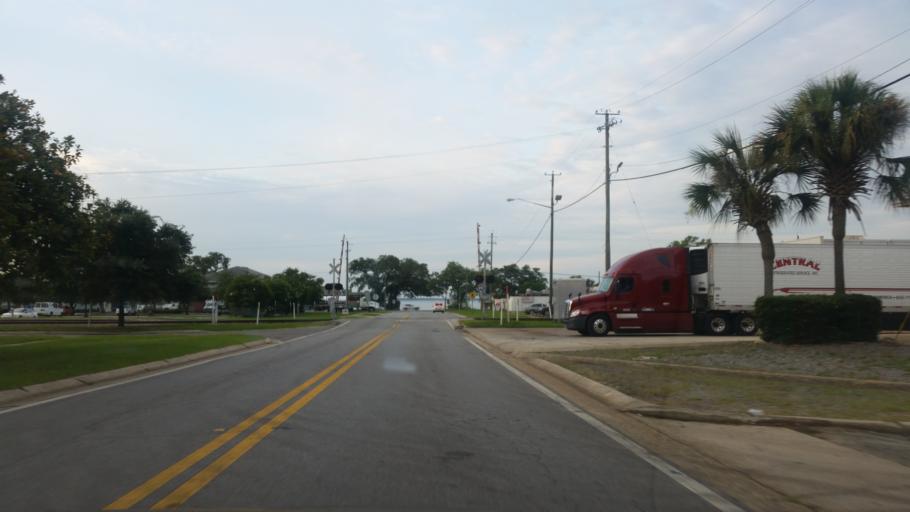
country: US
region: Florida
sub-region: Escambia County
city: Pensacola
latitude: 30.4203
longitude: -87.1988
